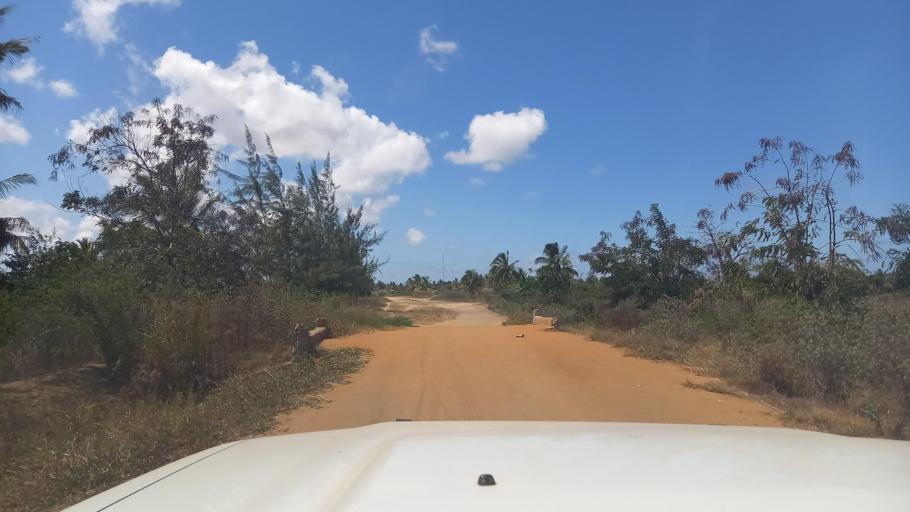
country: MZ
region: Cabo Delgado
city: Pemba
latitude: -13.4228
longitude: 40.5175
